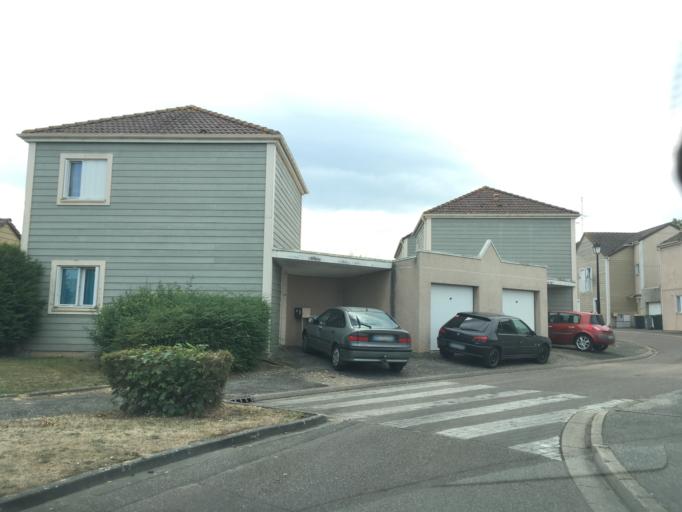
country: FR
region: Haute-Normandie
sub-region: Departement de l'Eure
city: Saint-Marcel
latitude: 49.1003
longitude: 1.4537
